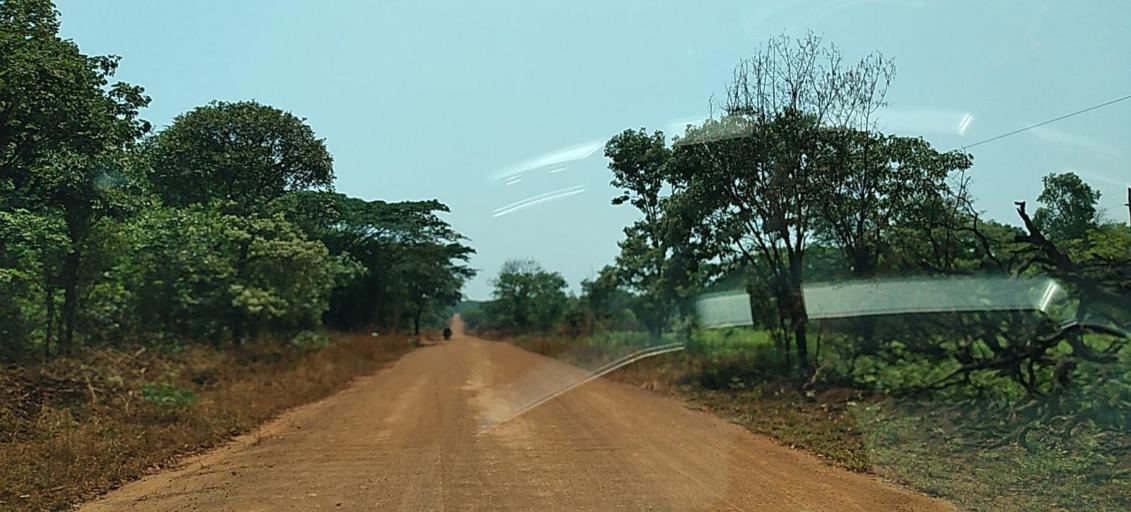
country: ZM
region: North-Western
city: Kansanshi
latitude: -11.9868
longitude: 26.8497
